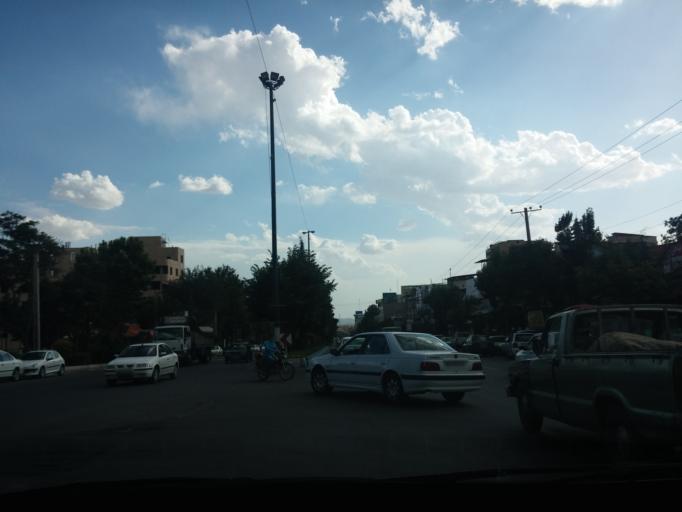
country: IR
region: Tehran
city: Damavand
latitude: 35.7335
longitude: 51.9067
